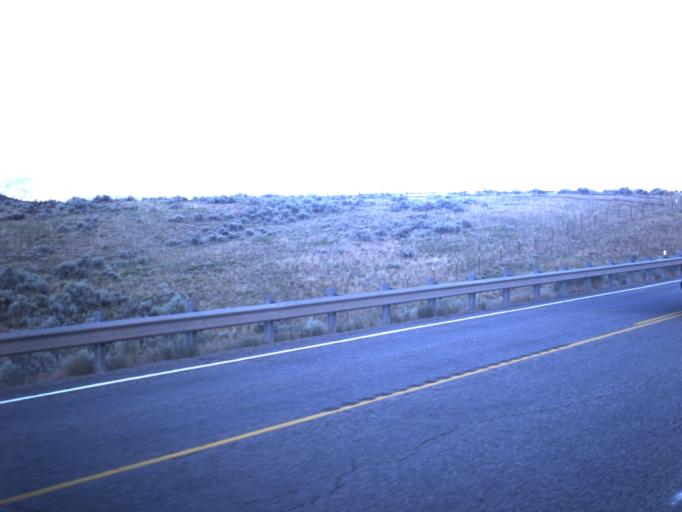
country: US
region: Utah
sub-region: Utah County
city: Woodland Hills
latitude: 39.8525
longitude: -111.5206
